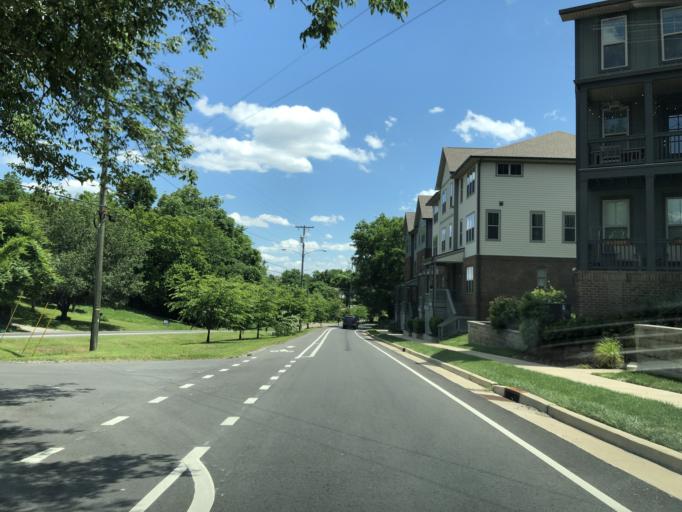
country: US
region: Tennessee
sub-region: Davidson County
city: Nashville
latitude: 36.1867
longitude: -86.7261
